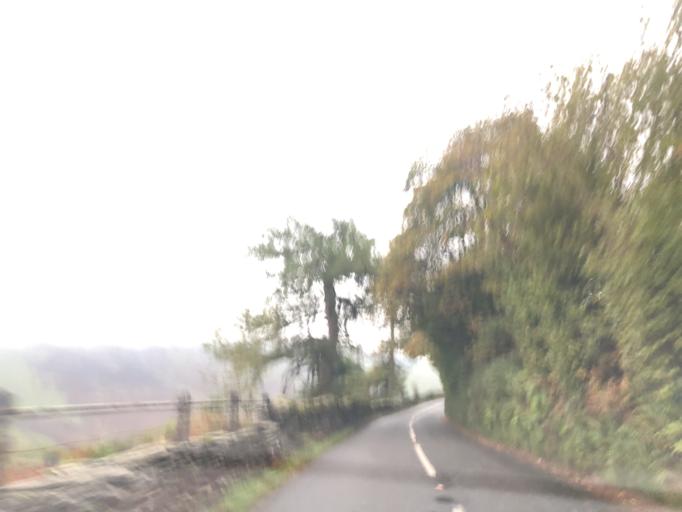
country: GB
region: England
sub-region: Cumbria
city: Windermere
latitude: 54.4377
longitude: -2.9020
